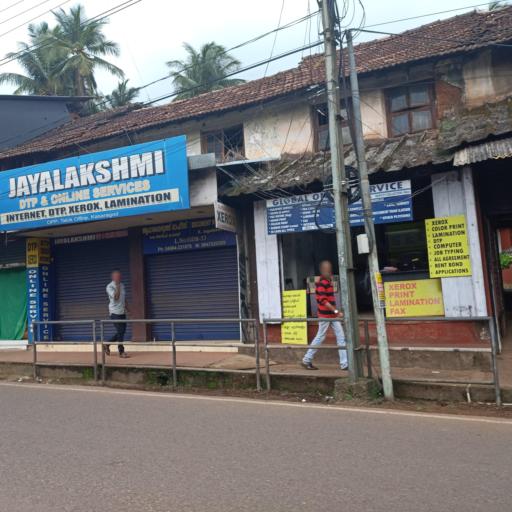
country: IN
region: Kerala
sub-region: Kasaragod District
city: Kasaragod
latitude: 12.4999
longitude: 74.9867
